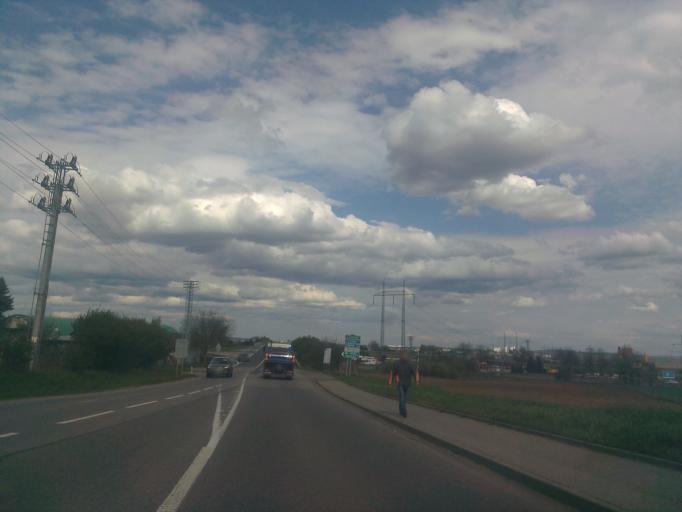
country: CZ
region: South Moravian
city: Modrice
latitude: 49.1218
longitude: 16.6012
